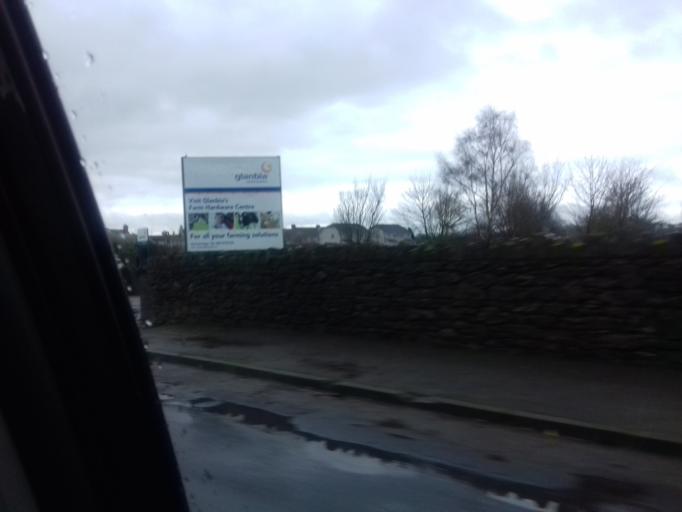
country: IE
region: Leinster
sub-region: County Carlow
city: Bagenalstown
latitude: 52.6282
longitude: -6.9932
